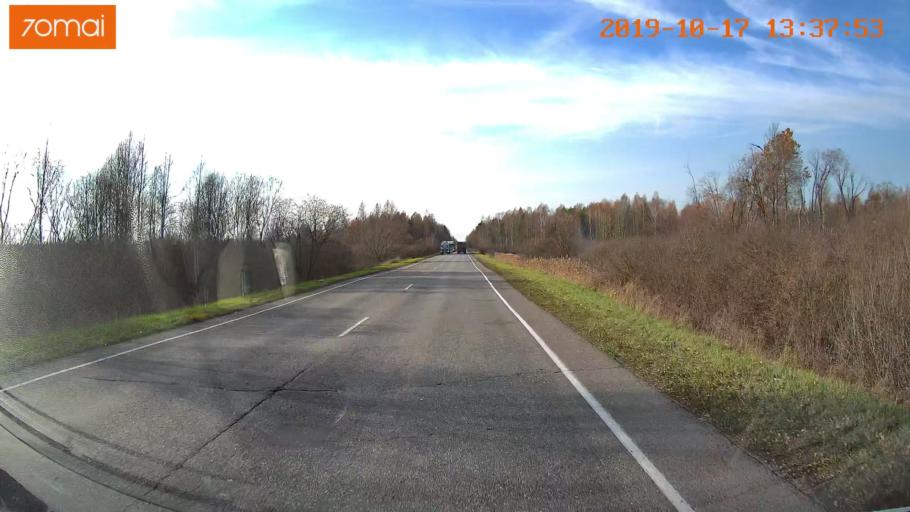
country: RU
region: Rjazan
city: Tuma
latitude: 55.1426
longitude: 40.6274
